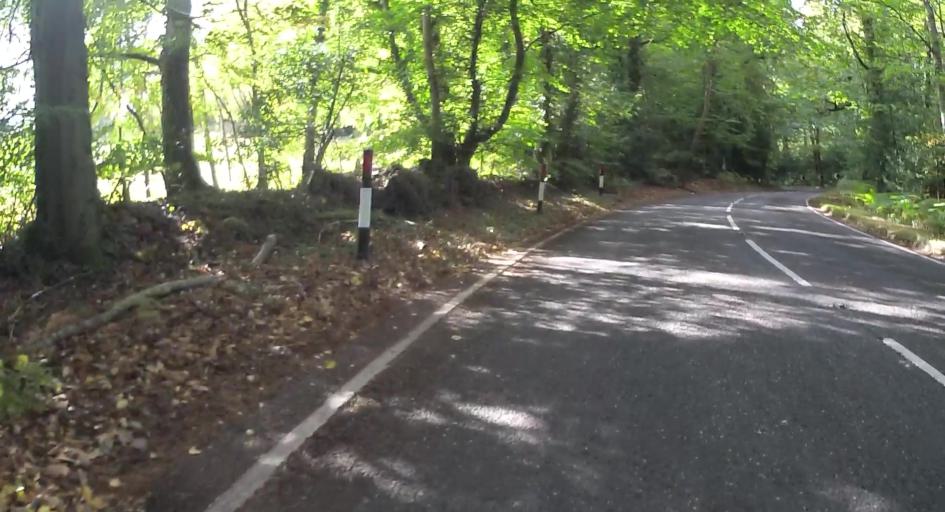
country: GB
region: England
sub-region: Surrey
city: Frimley
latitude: 51.2995
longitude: -0.7103
